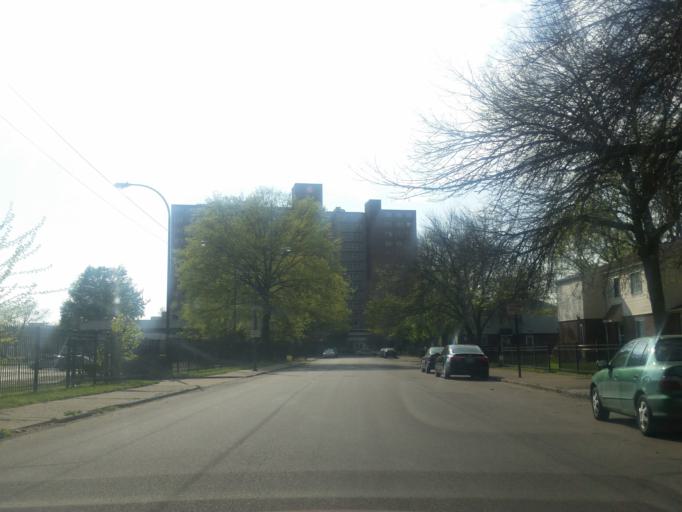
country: US
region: Ohio
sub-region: Cuyahoga County
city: Cleveland
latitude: 41.4957
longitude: -81.6647
